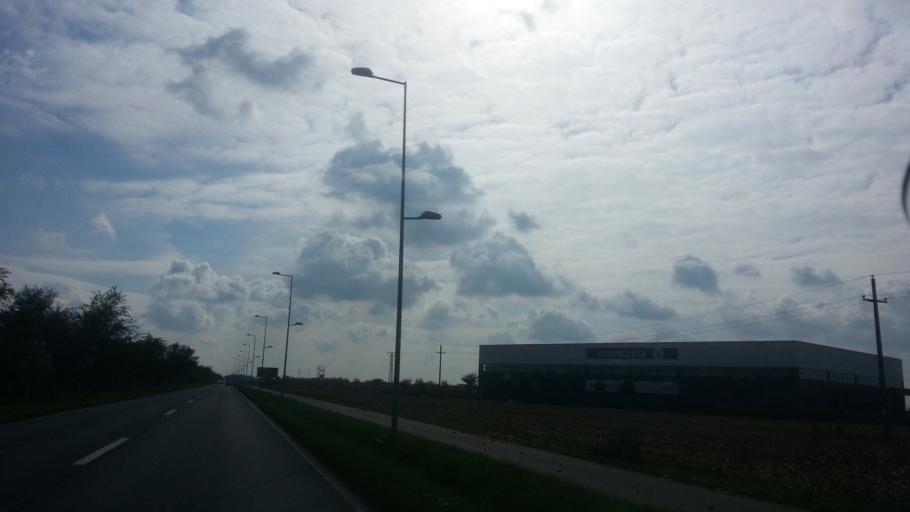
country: RS
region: Autonomna Pokrajina Vojvodina
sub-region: Sremski Okrug
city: Stara Pazova
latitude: 44.9665
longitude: 20.1843
